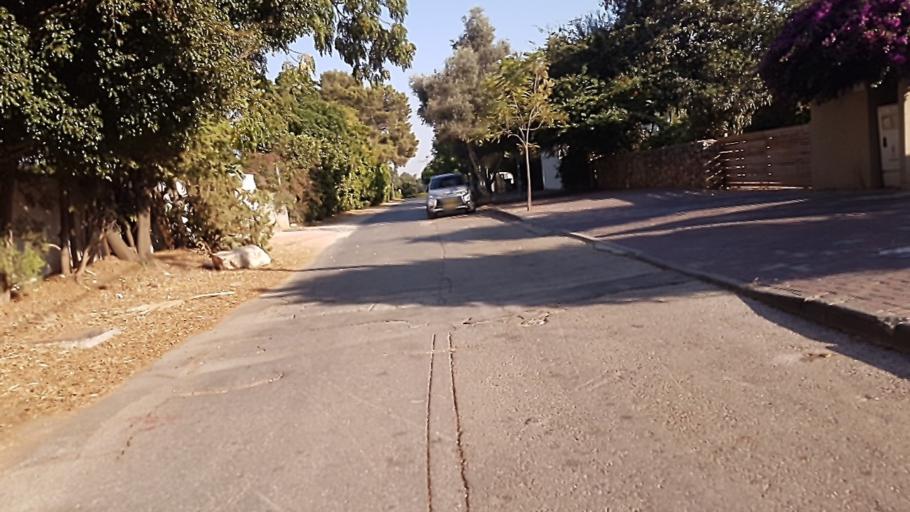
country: IL
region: Central District
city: Hod HaSharon
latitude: 32.1417
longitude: 34.9016
